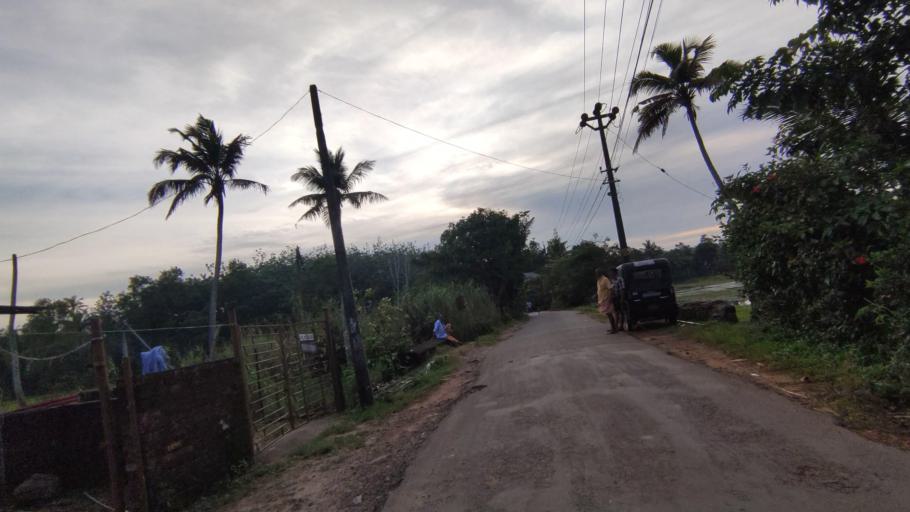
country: IN
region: Kerala
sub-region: Kottayam
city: Kottayam
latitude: 9.6345
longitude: 76.4991
